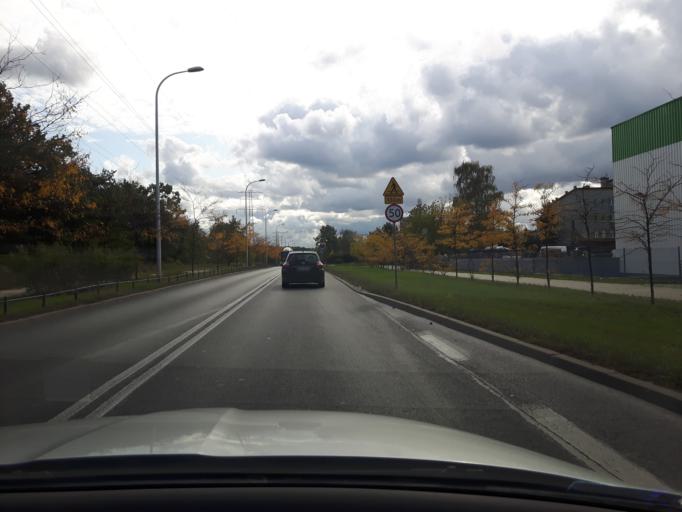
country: PL
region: Masovian Voivodeship
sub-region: Warszawa
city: Rembertow
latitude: 52.2409
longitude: 21.1402
